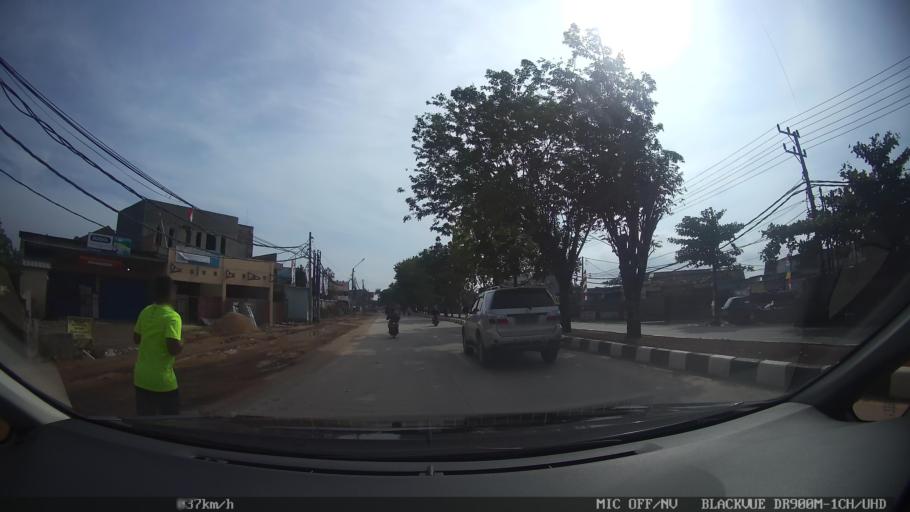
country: ID
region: Lampung
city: Kedaton
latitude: -5.3796
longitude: 105.2925
